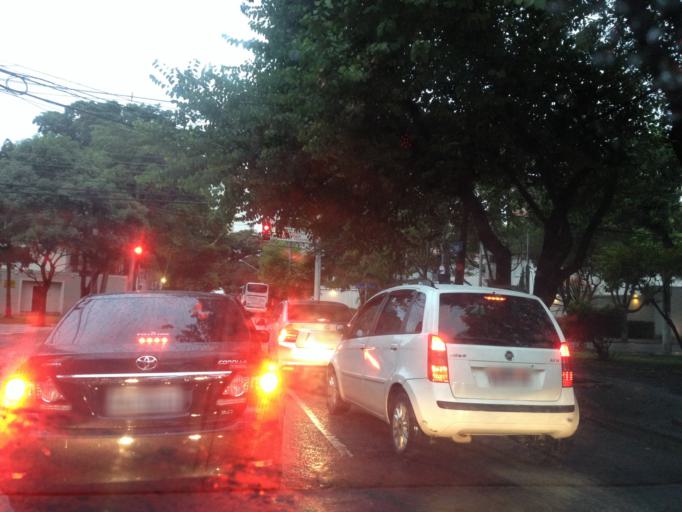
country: BR
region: Sao Paulo
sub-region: Sao Paulo
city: Sao Paulo
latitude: -23.5755
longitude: -46.6620
